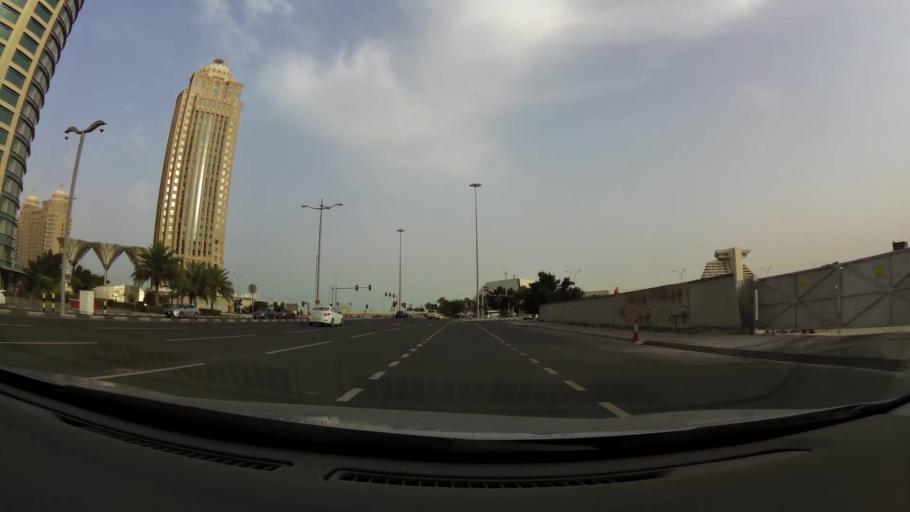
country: QA
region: Baladiyat ad Dawhah
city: Doha
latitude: 25.3236
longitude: 51.5352
